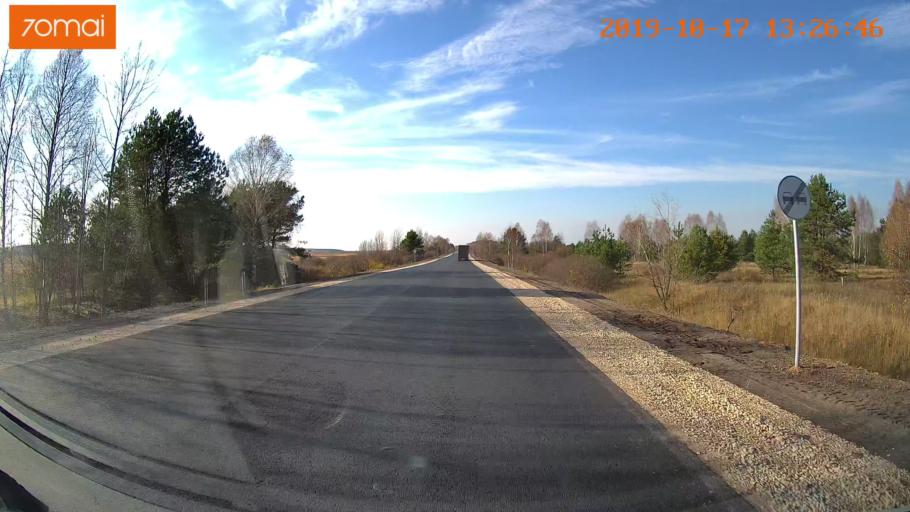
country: RU
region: Rjazan
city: Gus'-Zheleznyy
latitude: 55.1113
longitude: 40.9124
